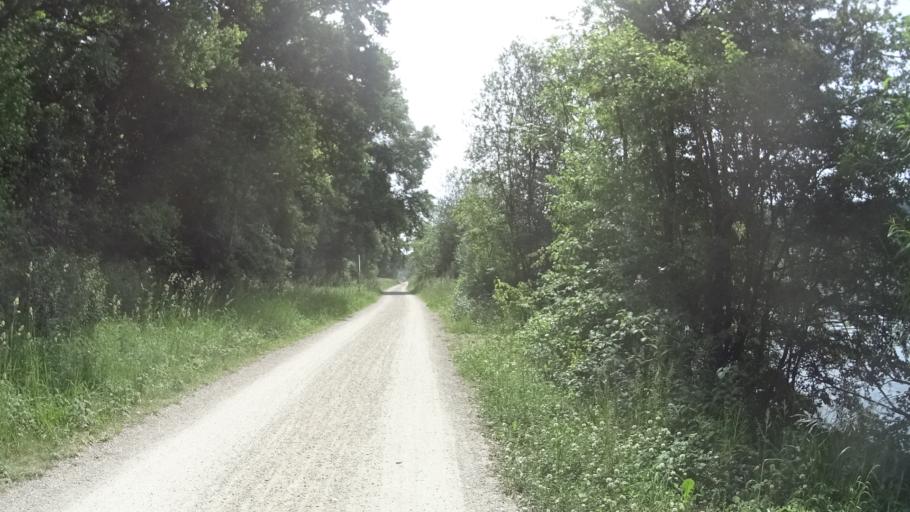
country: DE
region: Bavaria
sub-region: Lower Bavaria
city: Saal
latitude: 48.9096
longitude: 11.9392
